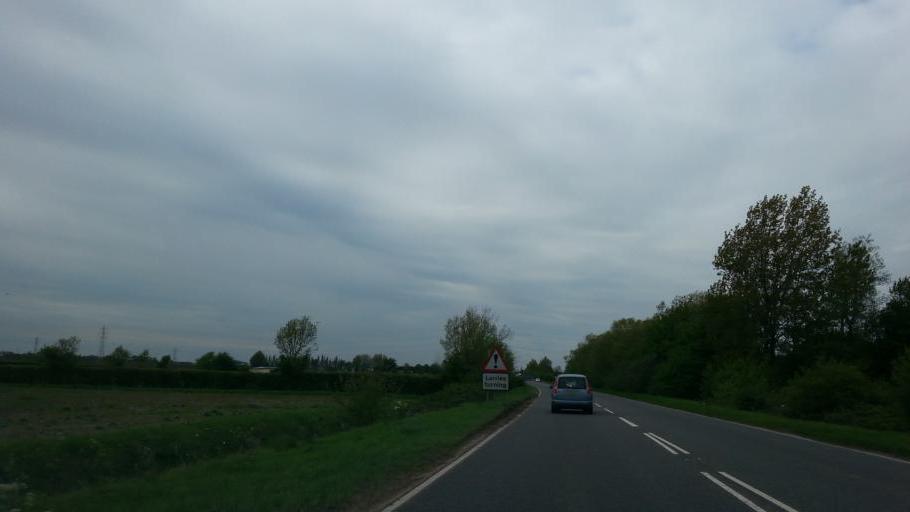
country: GB
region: England
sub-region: Cambridgeshire
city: March
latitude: 52.5472
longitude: 0.0703
